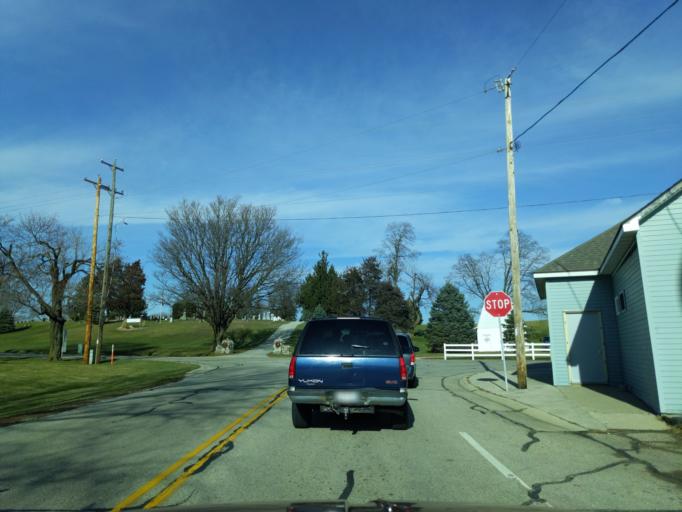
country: US
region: Wisconsin
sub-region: Walworth County
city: Elkhorn
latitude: 42.7341
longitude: -88.5822
